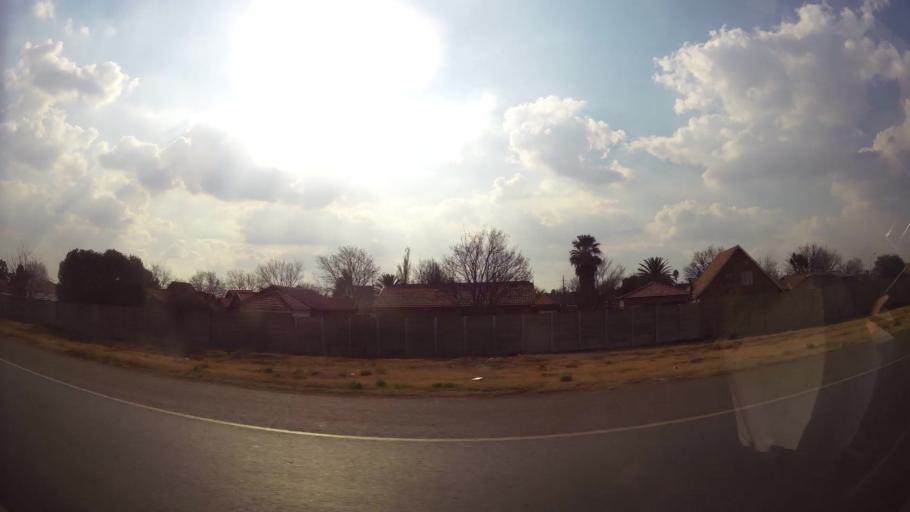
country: ZA
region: Gauteng
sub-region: Ekurhuleni Metropolitan Municipality
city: Germiston
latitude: -26.2936
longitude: 28.2154
